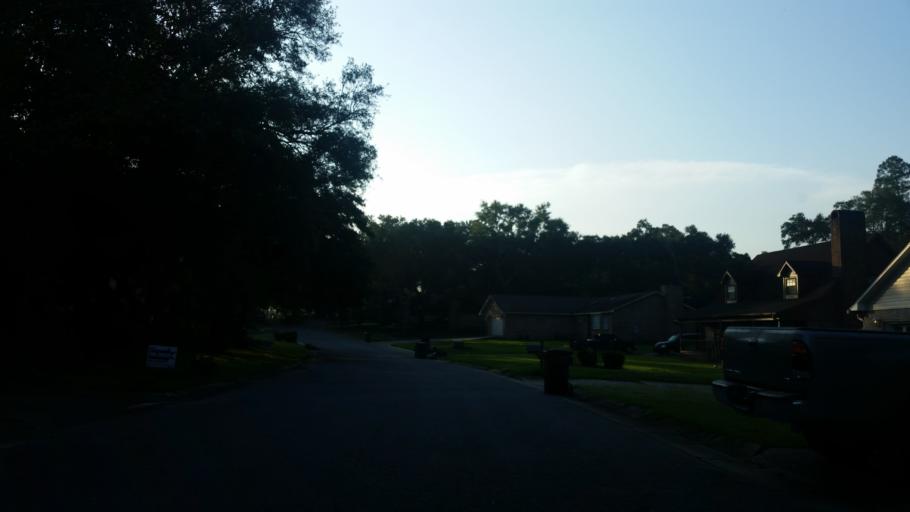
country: US
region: Florida
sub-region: Escambia County
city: Ferry Pass
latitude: 30.4978
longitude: -87.2351
